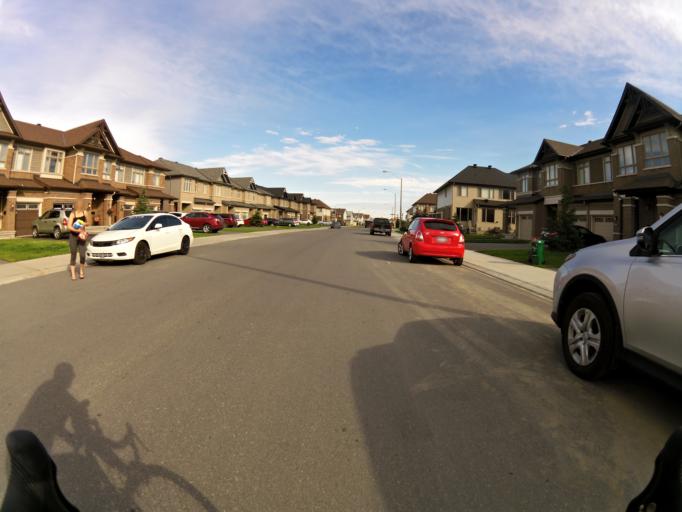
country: CA
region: Ontario
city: Bells Corners
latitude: 45.2705
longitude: -75.7798
